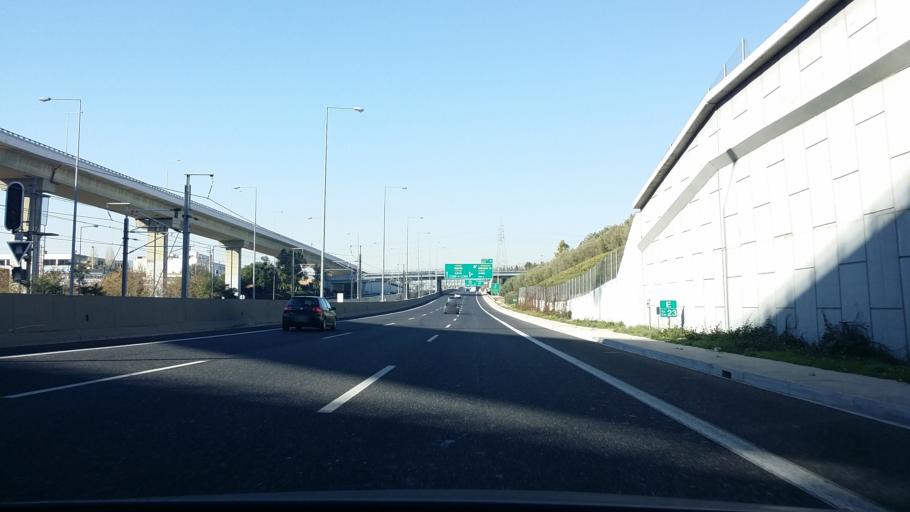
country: GR
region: Attica
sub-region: Nomarchia Athinas
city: Metamorfosi
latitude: 38.0622
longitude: 23.7494
